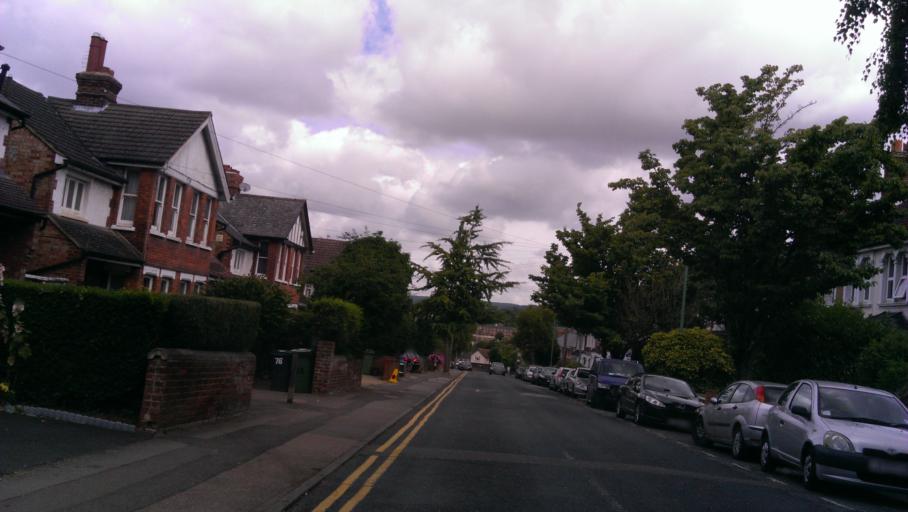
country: GB
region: England
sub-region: Kent
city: Maidstone
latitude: 51.2682
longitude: 0.5295
